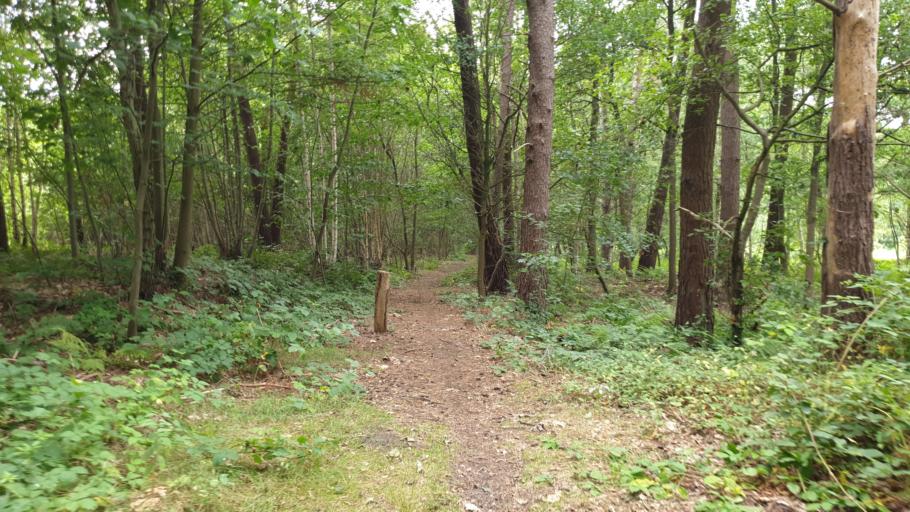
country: BE
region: Flanders
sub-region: Provincie Antwerpen
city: Meerhout
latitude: 51.1463
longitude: 5.0392
